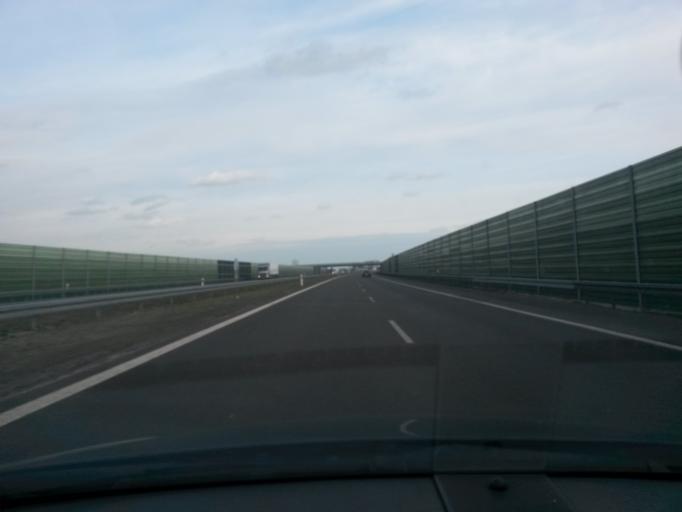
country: PL
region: Greater Poland Voivodeship
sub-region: Powiat kolski
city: Grzegorzew
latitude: 52.1143
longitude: 18.7333
